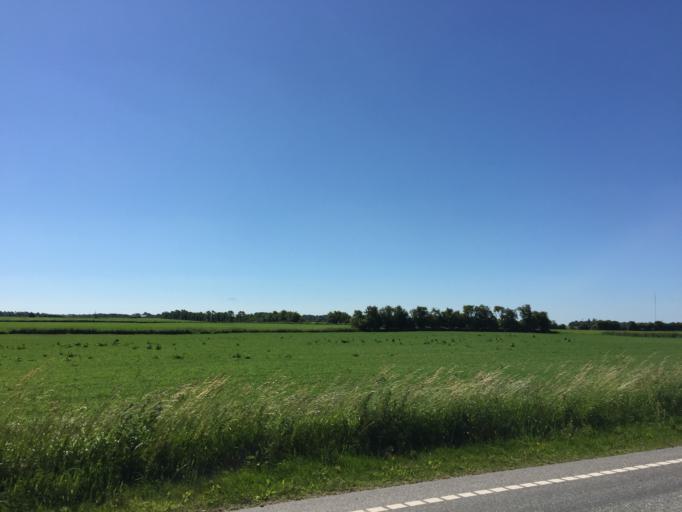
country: DK
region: South Denmark
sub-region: Aabenraa Kommune
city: Rodekro
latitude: 55.1488
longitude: 9.2272
